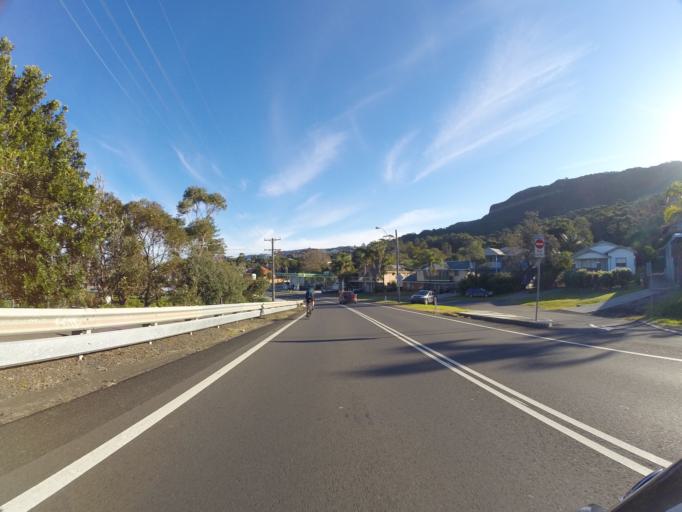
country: AU
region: New South Wales
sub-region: Wollongong
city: Bulli
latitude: -34.2998
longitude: 150.9399
